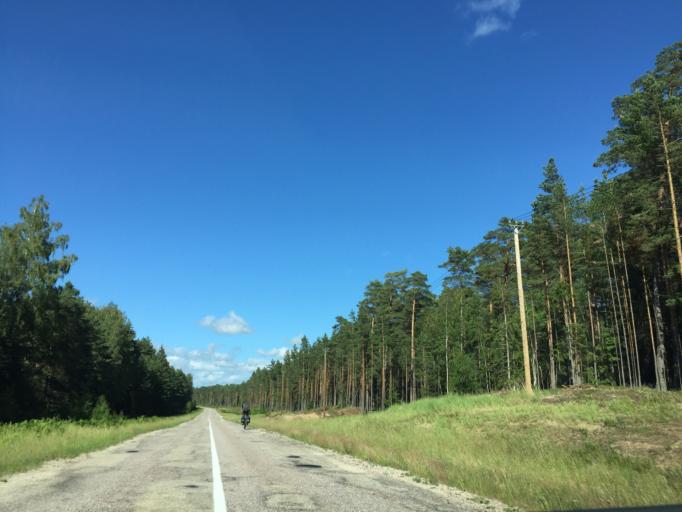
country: LV
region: Ventspils
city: Ventspils
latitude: 57.4721
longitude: 21.6614
